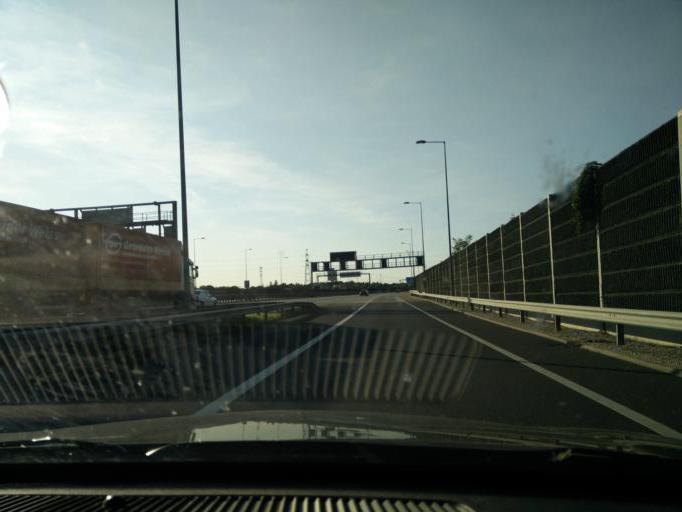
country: HU
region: Pest
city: Diosd
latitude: 47.4028
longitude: 18.9718
